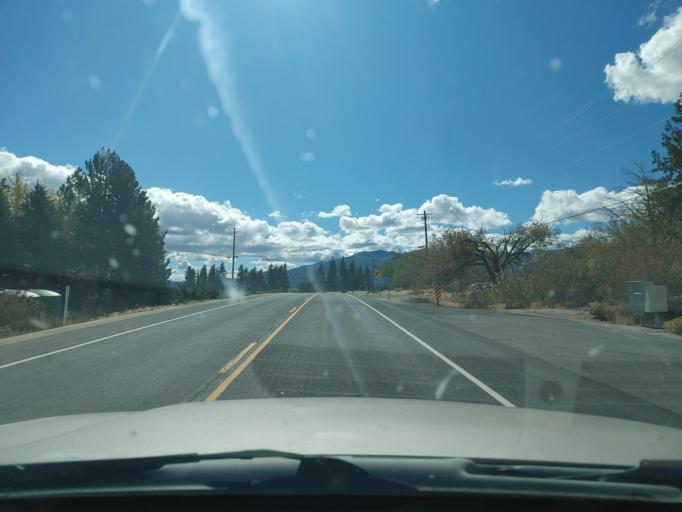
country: US
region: Nevada
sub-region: Carson City
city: Carson City
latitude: 39.2953
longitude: -119.8294
